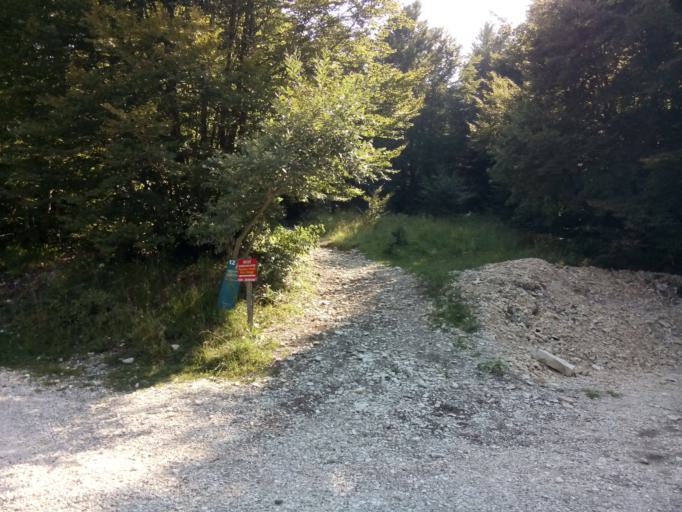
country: IT
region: Veneto
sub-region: Provincia di Vicenza
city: Valstagna
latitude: 45.8317
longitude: 11.6349
